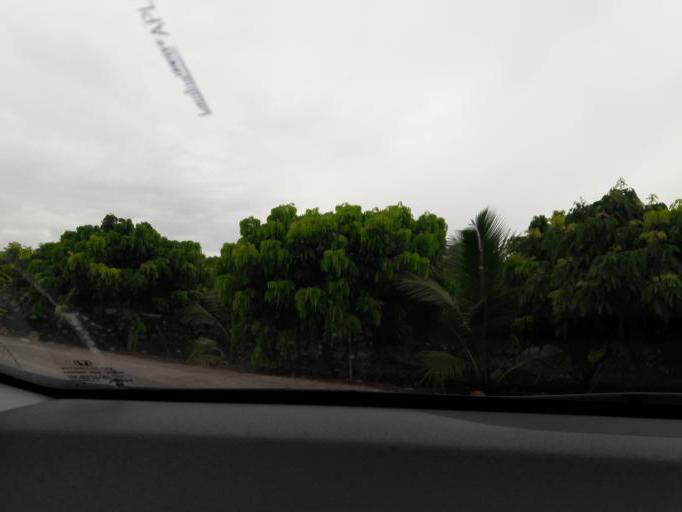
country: TH
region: Ratchaburi
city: Damnoen Saduak
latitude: 13.5616
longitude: 100.0093
